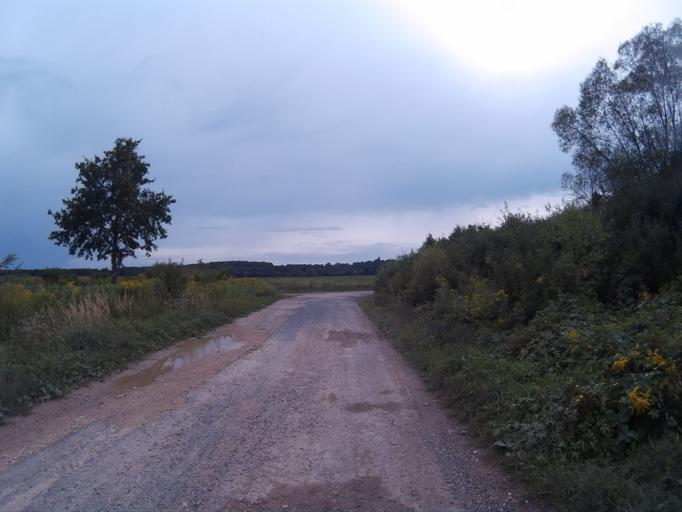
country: SI
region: Kobilje
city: Kobilje
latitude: 46.7333
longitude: 16.4373
